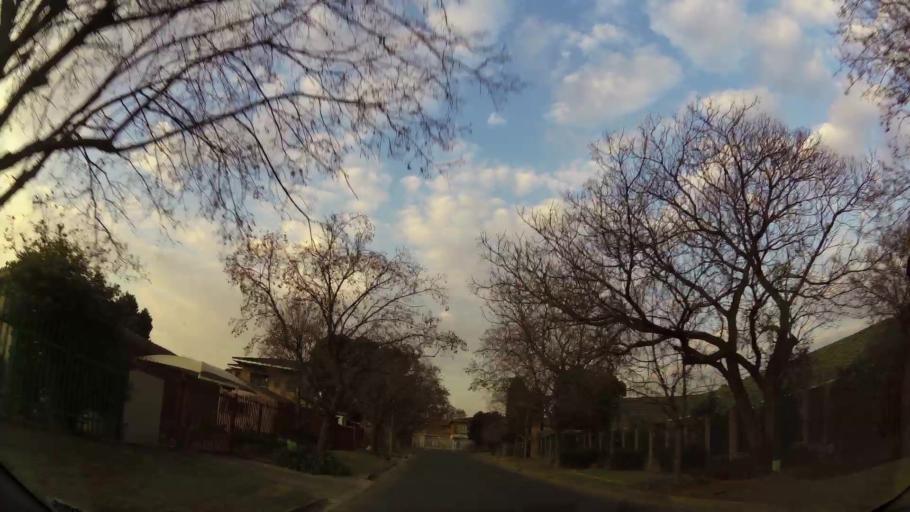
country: ZA
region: Gauteng
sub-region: Ekurhuleni Metropolitan Municipality
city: Benoni
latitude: -26.1639
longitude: 28.3050
